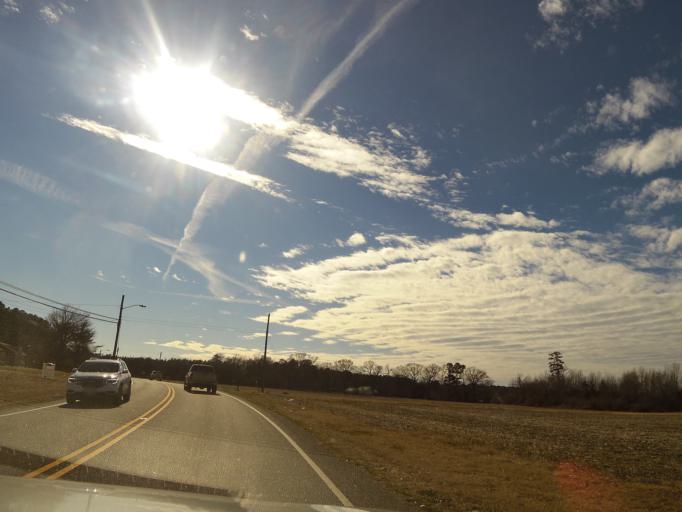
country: US
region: Virginia
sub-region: City of Franklin
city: Franklin
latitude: 36.7681
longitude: -76.8553
